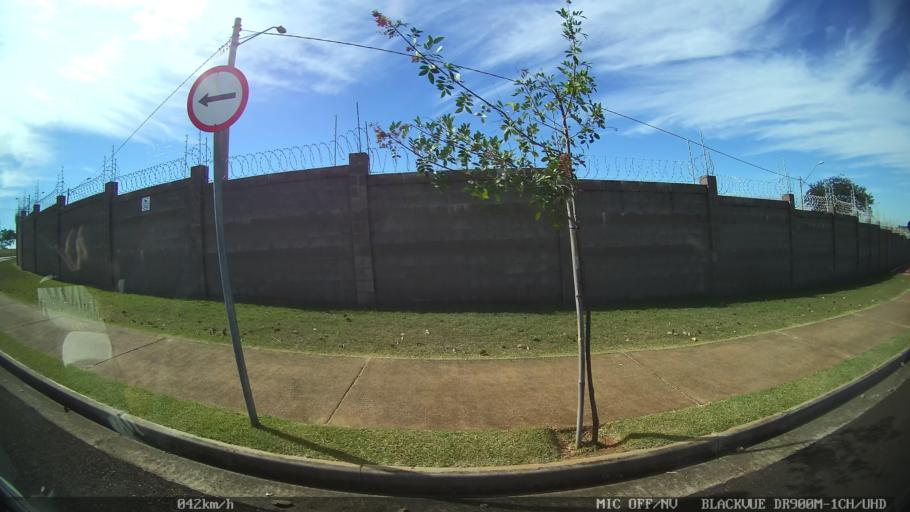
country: BR
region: Sao Paulo
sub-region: Sao Jose Do Rio Preto
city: Sao Jose do Rio Preto
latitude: -20.8542
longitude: -49.3747
